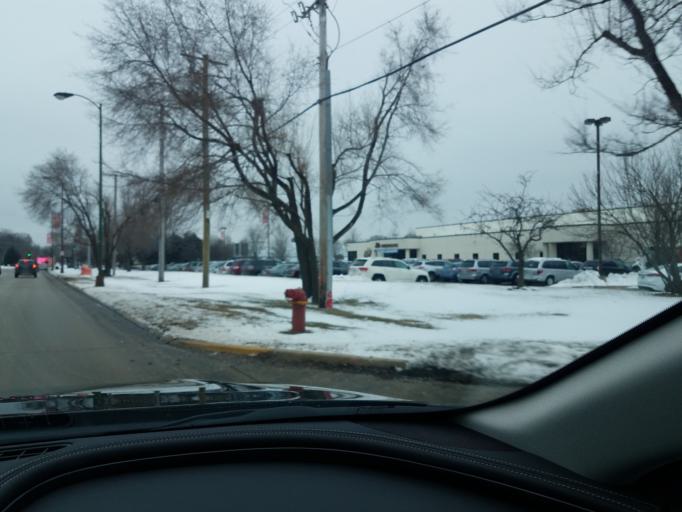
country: US
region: Illinois
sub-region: Cook County
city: Harwood Heights
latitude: 41.9593
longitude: -87.7957
